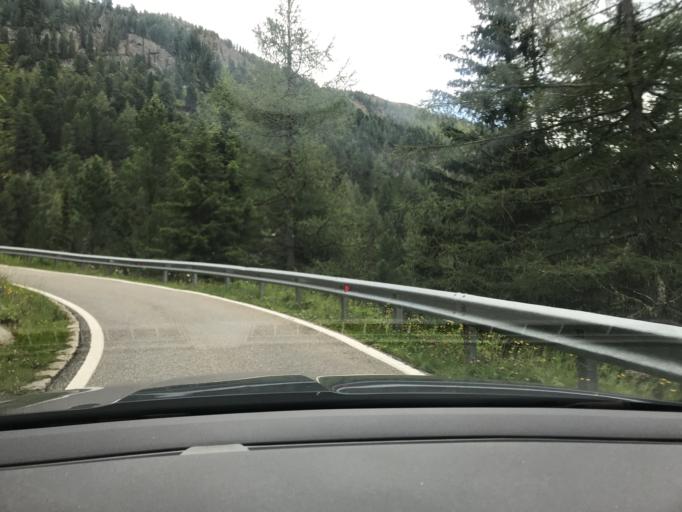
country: IT
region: Trentino-Alto Adige
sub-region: Bolzano
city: San Martino
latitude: 46.8882
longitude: 12.1948
